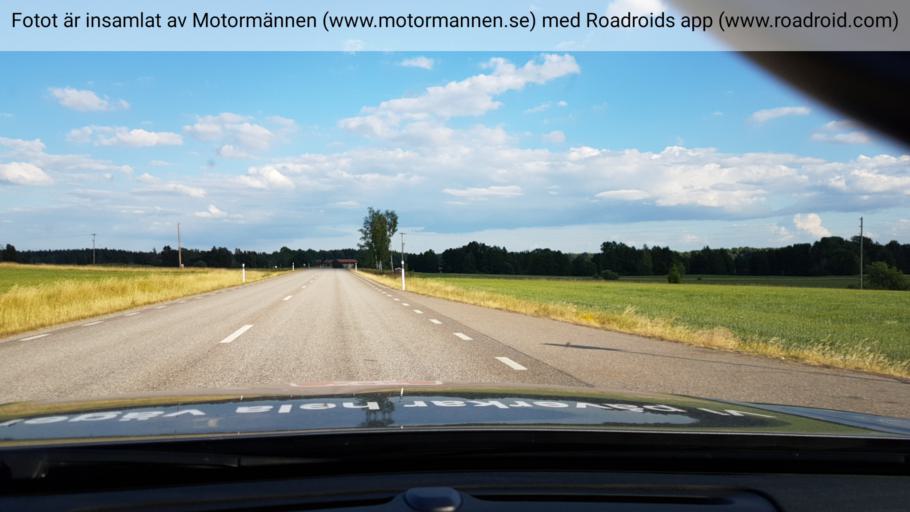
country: SE
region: Uppsala
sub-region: Heby Kommun
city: Morgongava
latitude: 59.8854
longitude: 16.9134
